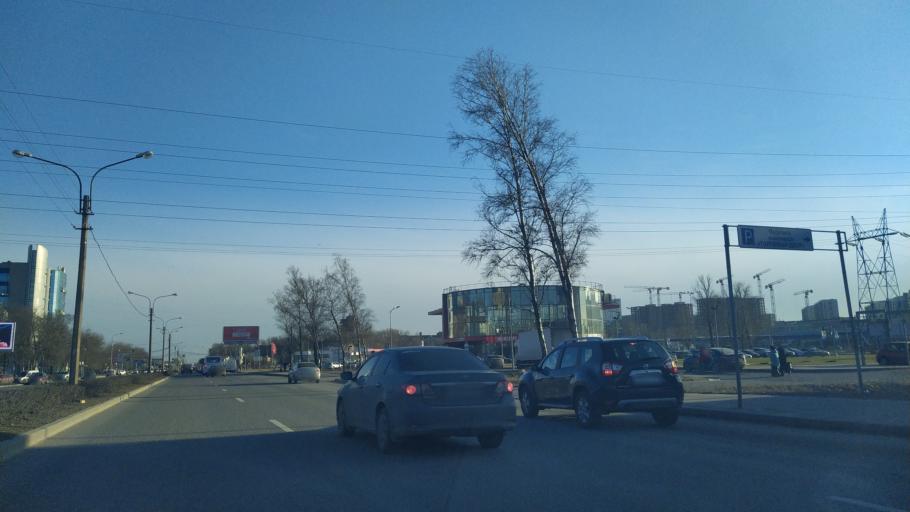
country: RU
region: St.-Petersburg
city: Kupchino
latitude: 59.8328
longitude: 30.3407
